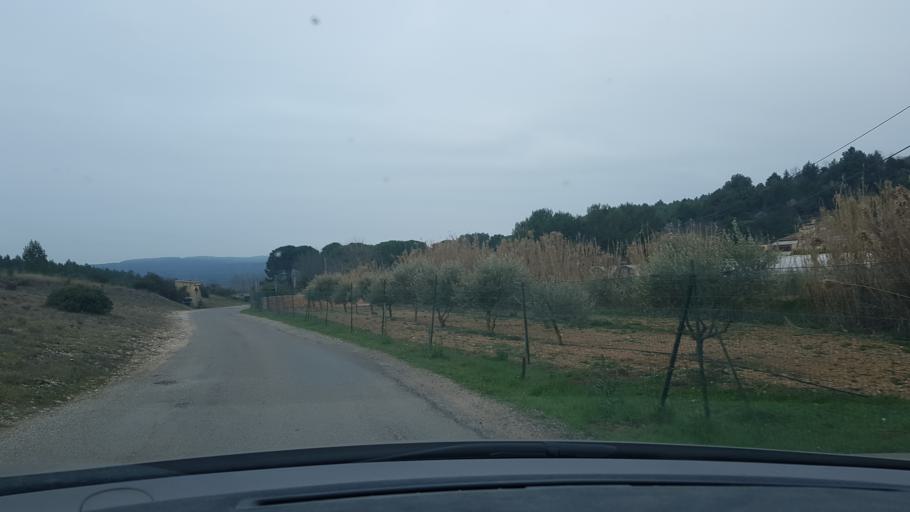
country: FR
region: Provence-Alpes-Cote d'Azur
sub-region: Departement des Bouches-du-Rhone
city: Meyreuil
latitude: 43.4818
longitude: 5.4706
